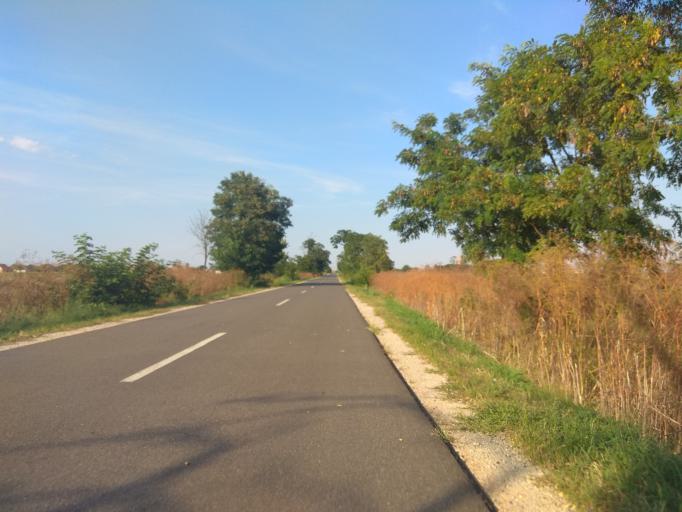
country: HU
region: Borsod-Abauj-Zemplen
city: Emod
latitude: 47.8812
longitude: 20.7658
